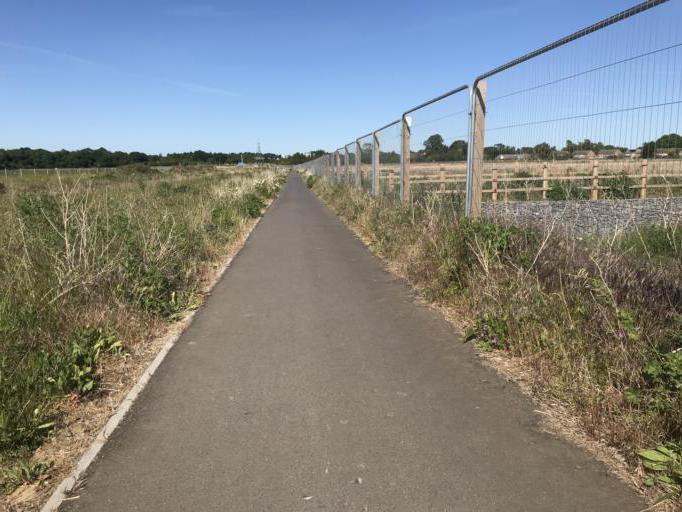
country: GB
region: England
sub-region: Cambridgeshire
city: Girton
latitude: 52.2284
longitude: 0.1040
